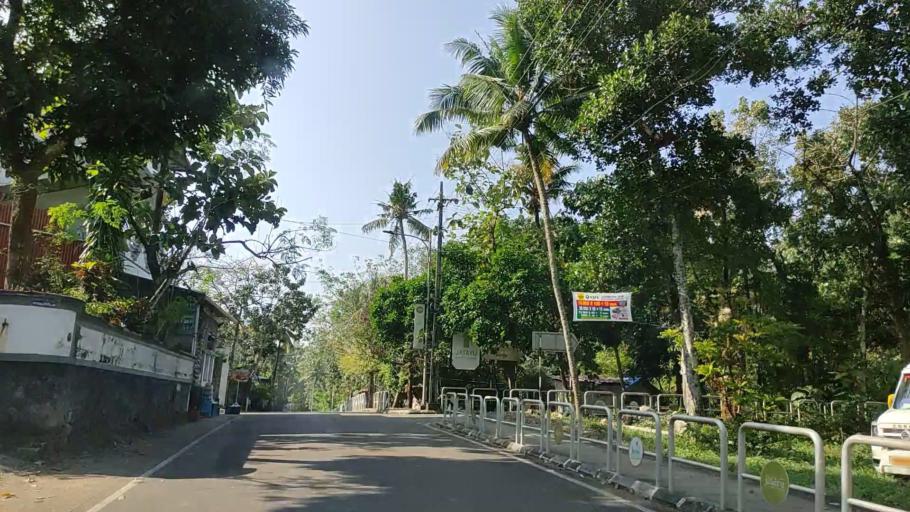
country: IN
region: Kerala
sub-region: Kollam
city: Punalur
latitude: 8.8633
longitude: 76.8699
